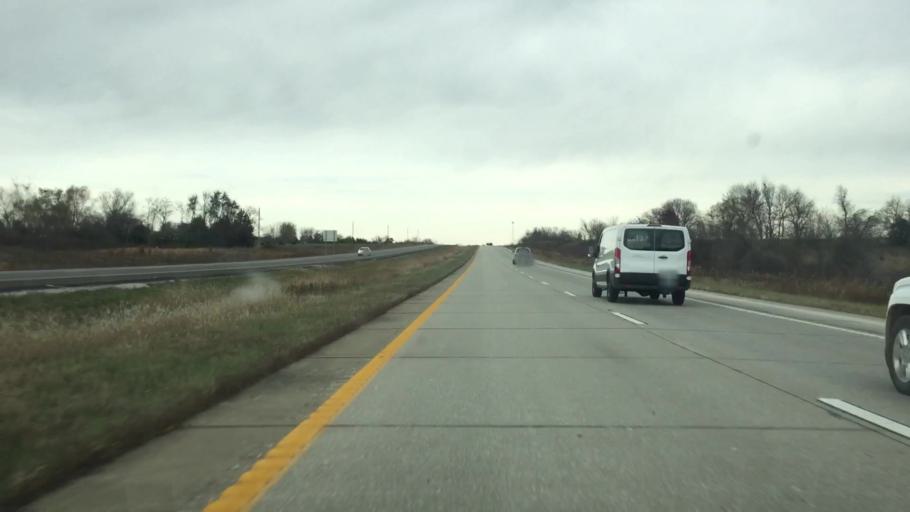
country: US
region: Missouri
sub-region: Saint Clair County
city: Osceola
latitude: 38.1132
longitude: -93.7062
